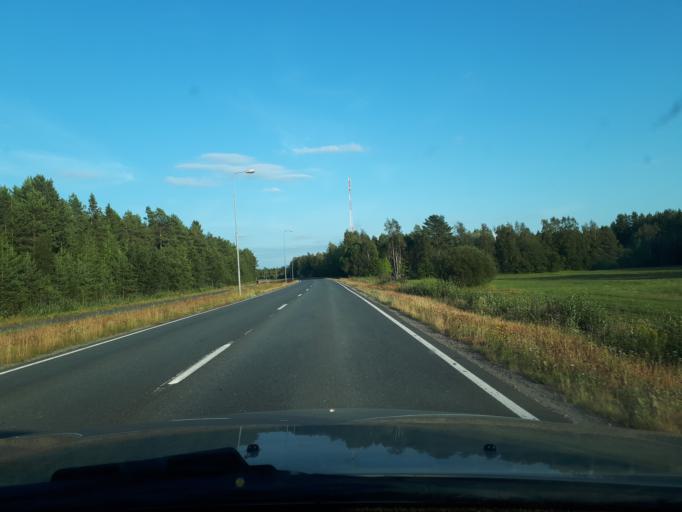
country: FI
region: Northern Ostrobothnia
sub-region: Oulu
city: Oulunsalo
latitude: 64.9769
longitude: 25.2824
